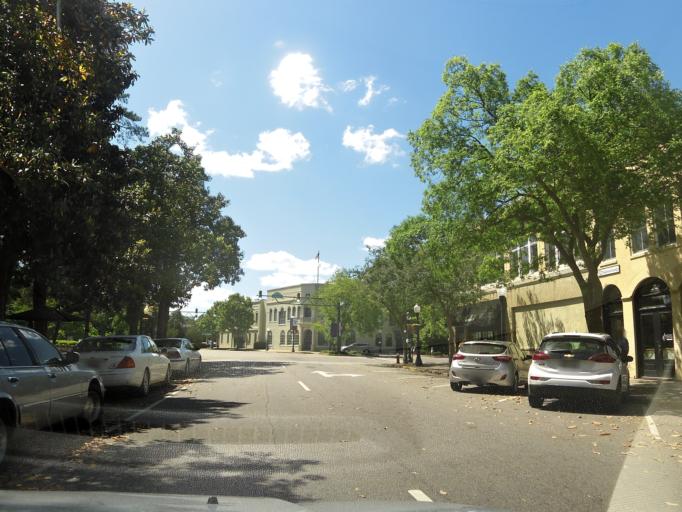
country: US
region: South Carolina
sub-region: Aiken County
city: Aiken
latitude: 33.5596
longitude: -81.7227
